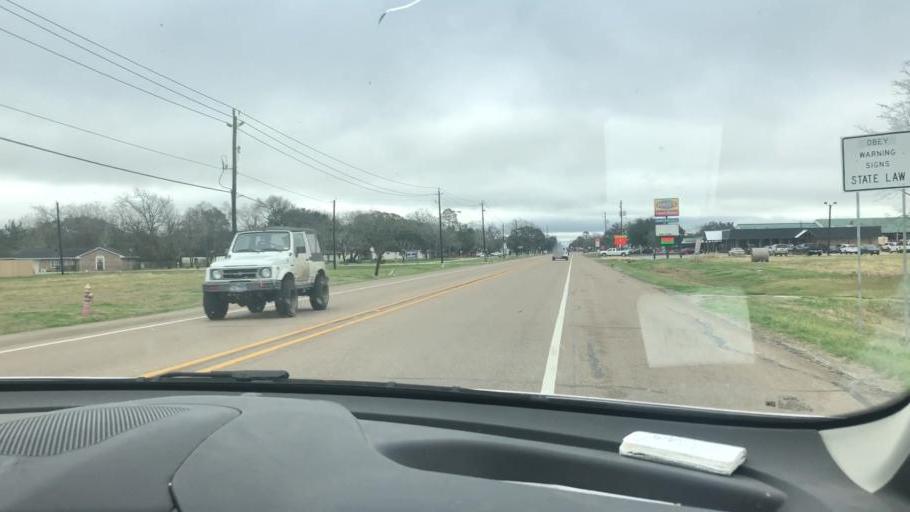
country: US
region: Texas
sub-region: Wharton County
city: Wharton
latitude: 29.3075
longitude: -96.0875
